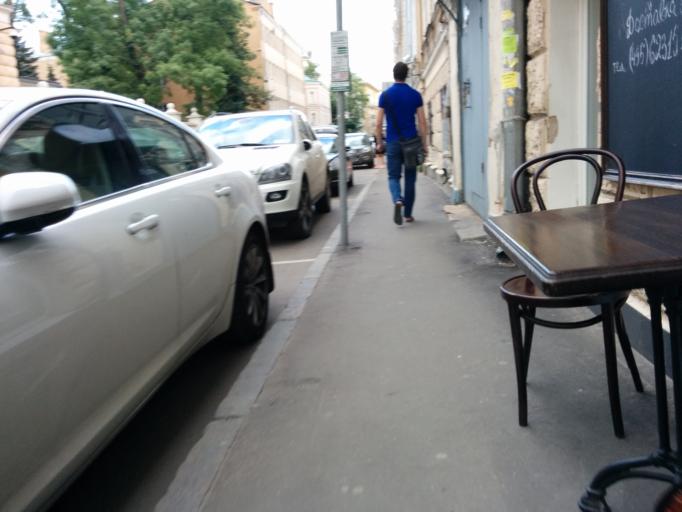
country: RU
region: Moscow
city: Moscow
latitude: 55.7639
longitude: 37.6463
